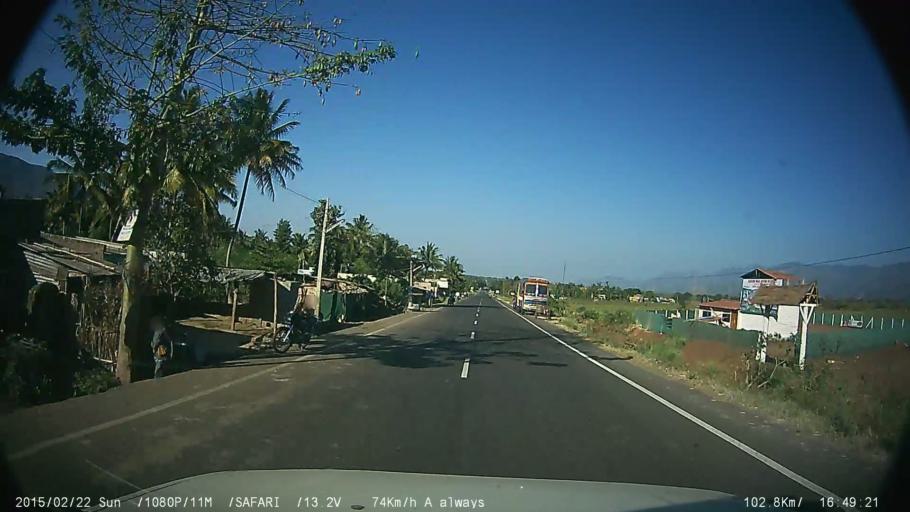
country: IN
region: Tamil Nadu
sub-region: Theni
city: Gudalur
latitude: 9.6315
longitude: 77.2009
